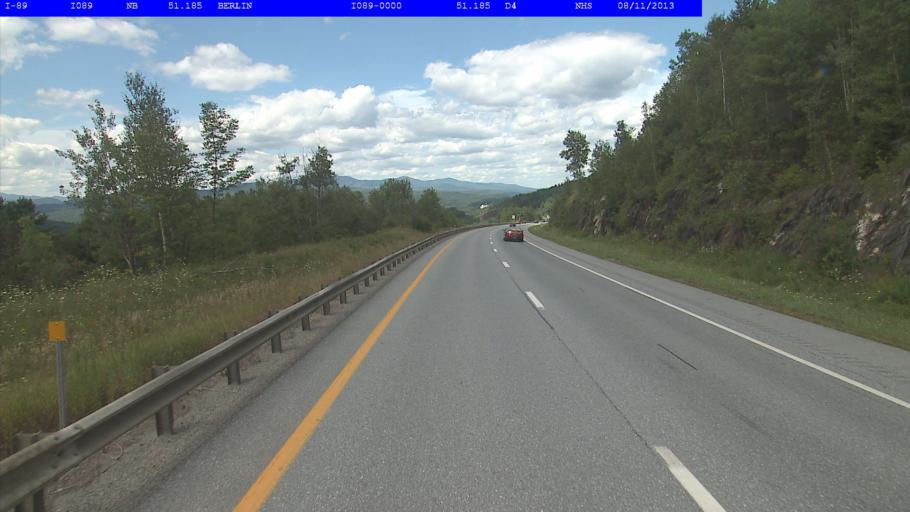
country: US
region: Vermont
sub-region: Washington County
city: Montpelier
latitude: 44.2287
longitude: -72.5862
